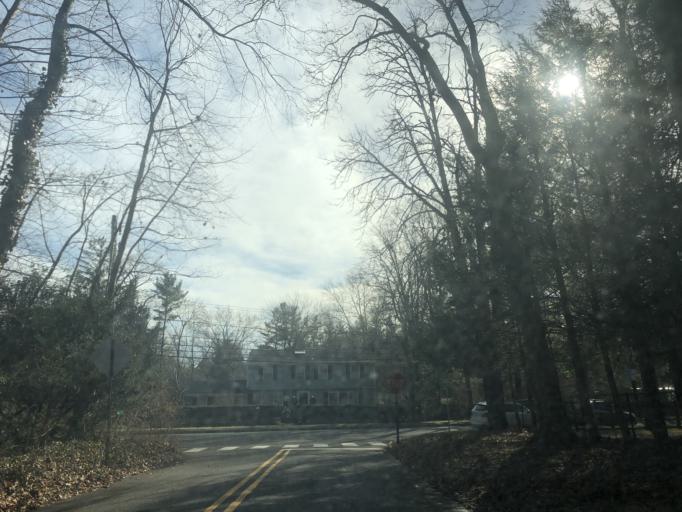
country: US
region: New Jersey
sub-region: Mercer County
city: Princeton
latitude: 40.3555
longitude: -74.6350
